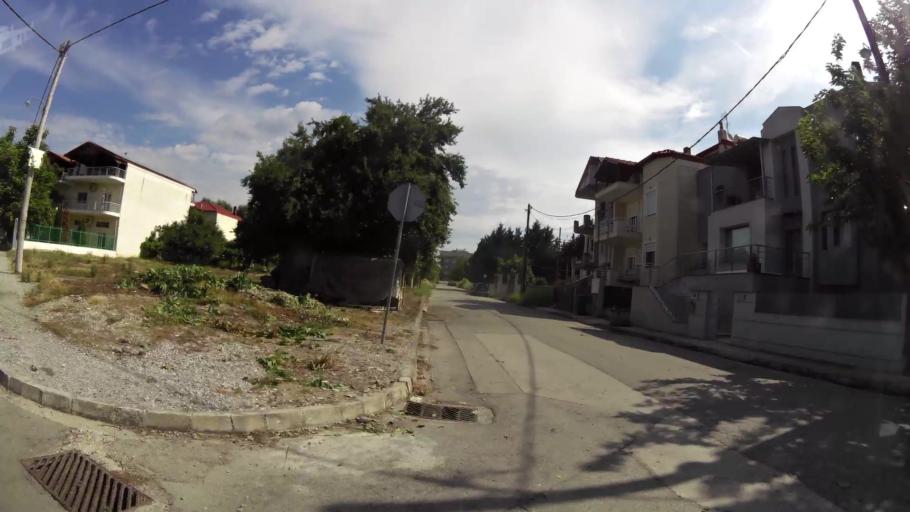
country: GR
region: Central Macedonia
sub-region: Nomos Pierias
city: Katerini
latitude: 40.2832
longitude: 22.5017
